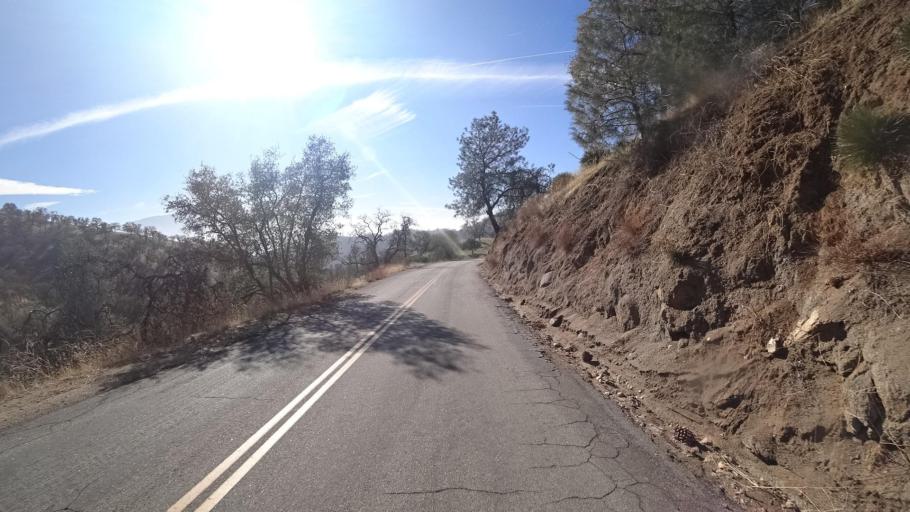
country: US
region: California
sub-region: Kern County
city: Bear Valley Springs
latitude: 35.3318
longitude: -118.5845
